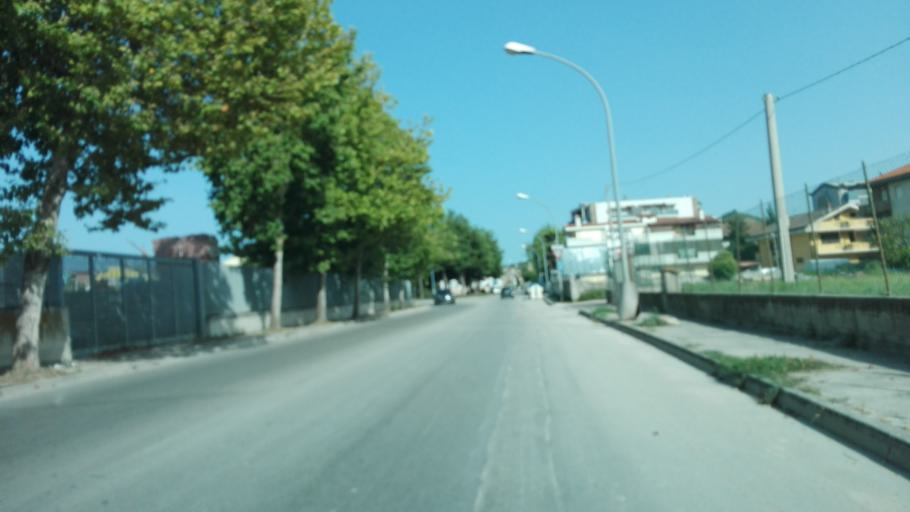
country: IT
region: Abruzzo
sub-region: Provincia di Pescara
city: Montesilvano Marina
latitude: 42.5131
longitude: 14.1394
